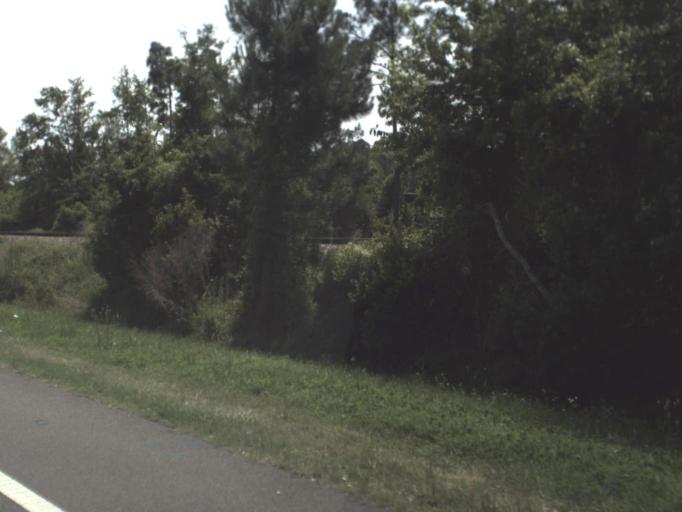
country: US
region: Florida
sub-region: Duval County
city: Jacksonville
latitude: 30.4737
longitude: -81.6306
